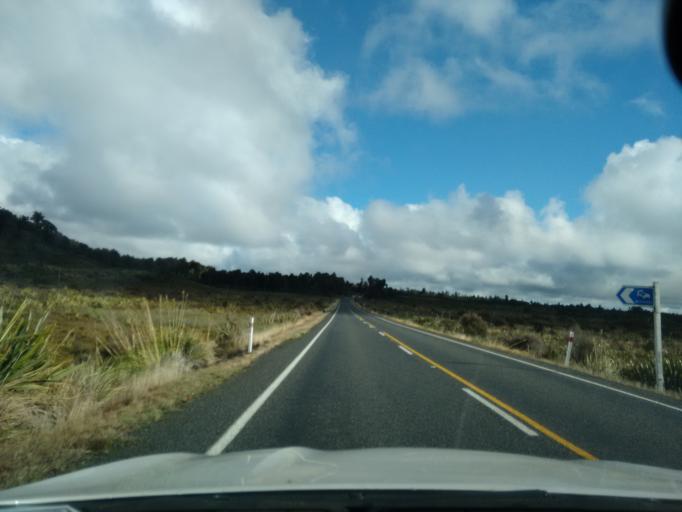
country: NZ
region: Manawatu-Wanganui
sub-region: Ruapehu District
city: Waiouru
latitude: -39.2282
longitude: 175.3956
